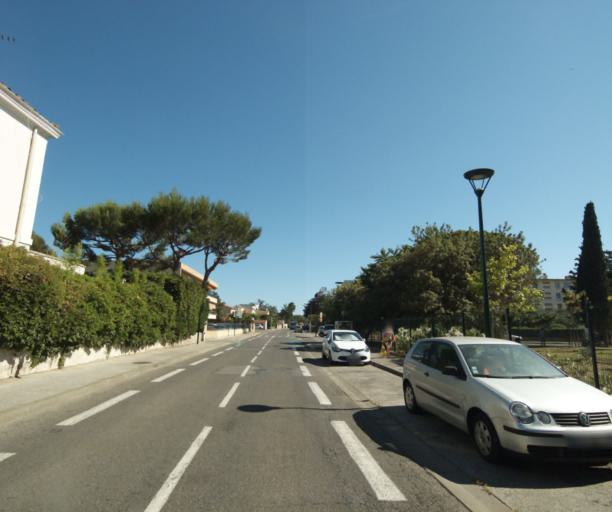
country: FR
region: Provence-Alpes-Cote d'Azur
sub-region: Departement du Var
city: La Garde
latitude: 43.1212
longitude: 6.0051
